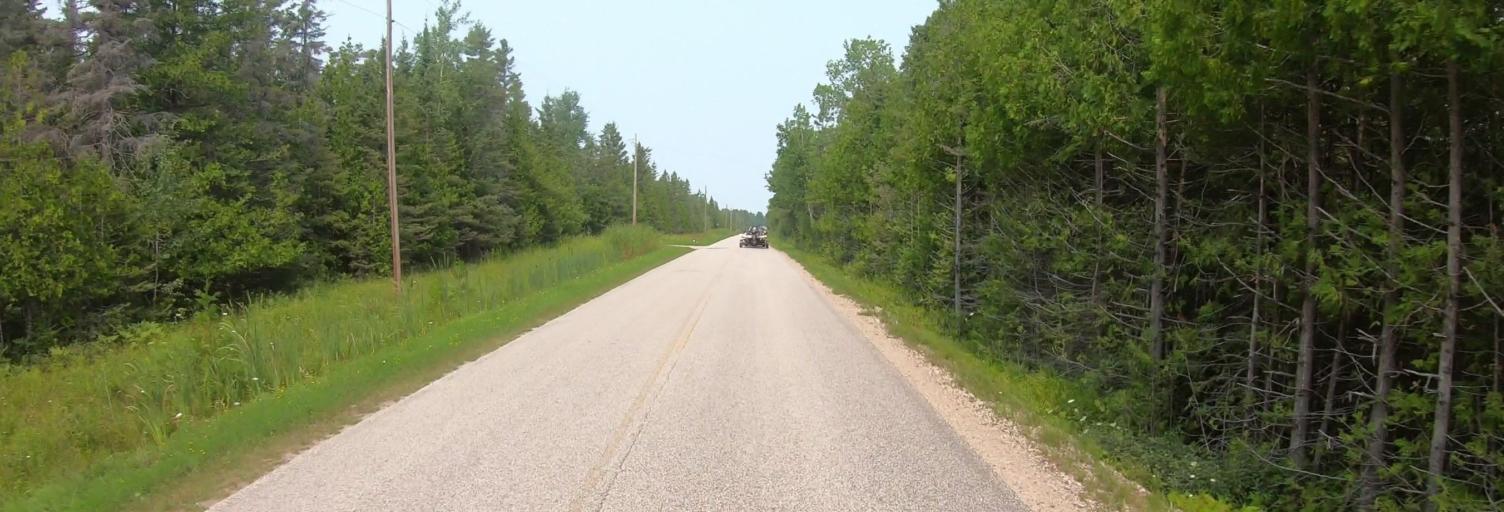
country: CA
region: Ontario
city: Thessalon
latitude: 46.0434
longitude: -83.6663
